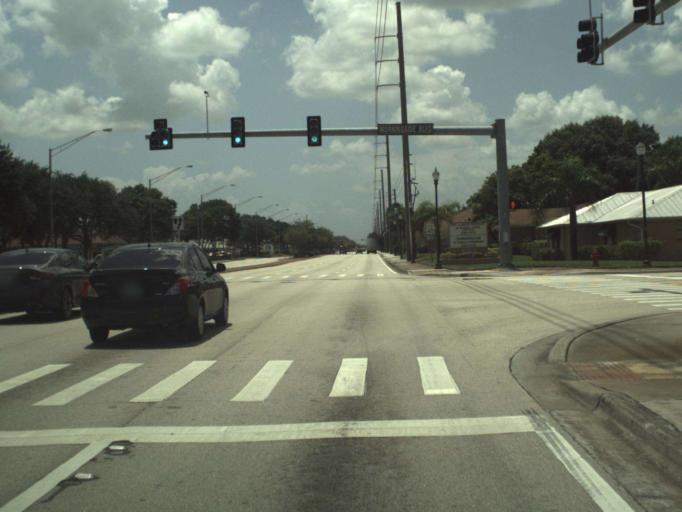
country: US
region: Florida
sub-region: Saint Lucie County
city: Port Saint Lucie
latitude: 27.2712
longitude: -80.2973
